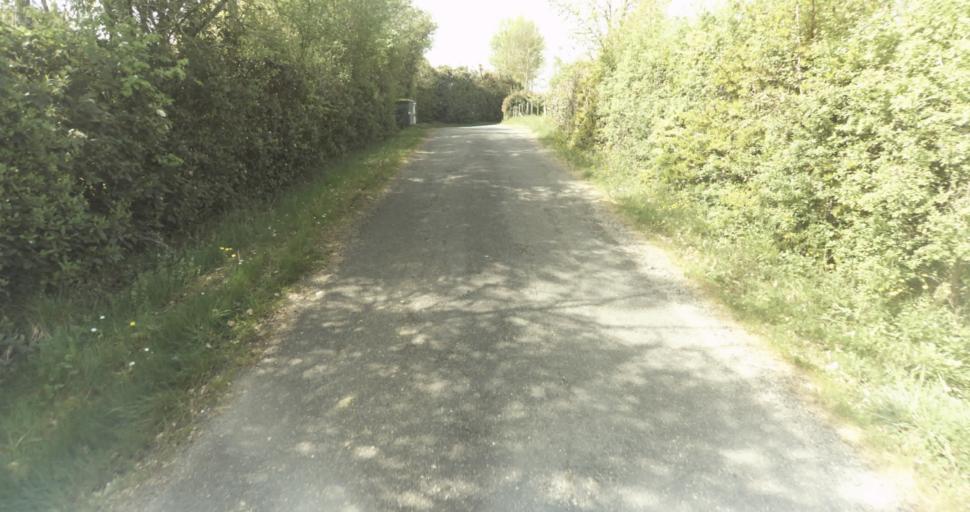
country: FR
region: Midi-Pyrenees
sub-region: Departement du Tarn-et-Garonne
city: Moissac
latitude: 44.1390
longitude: 1.0944
